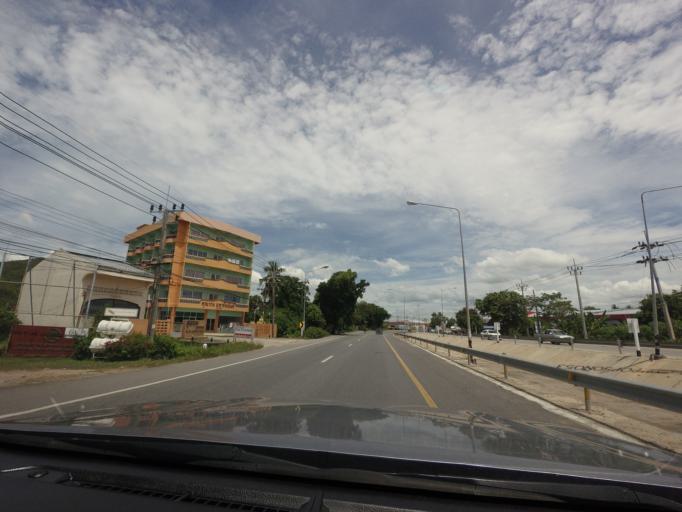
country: TH
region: Songkhla
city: Ban Mai
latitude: 7.2119
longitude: 100.5572
